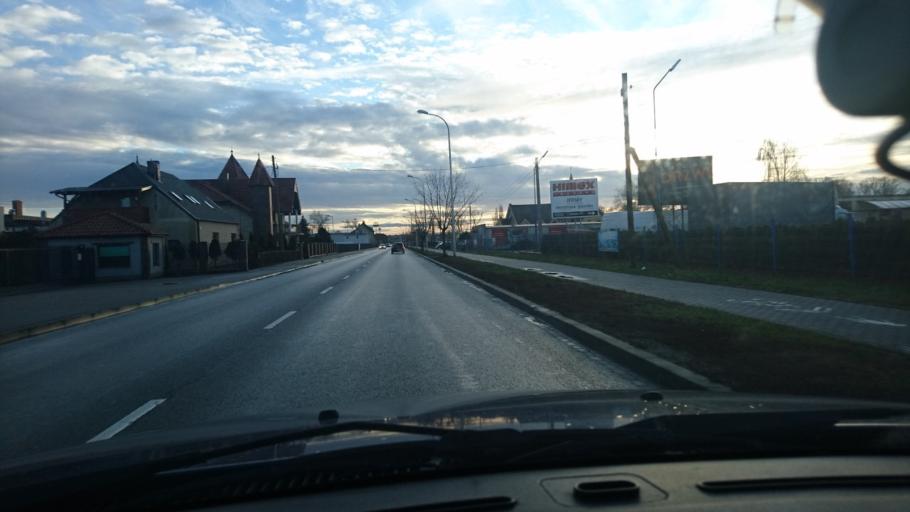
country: PL
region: Greater Poland Voivodeship
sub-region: Powiat kepinski
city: Kepno
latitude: 51.2936
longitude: 17.9956
